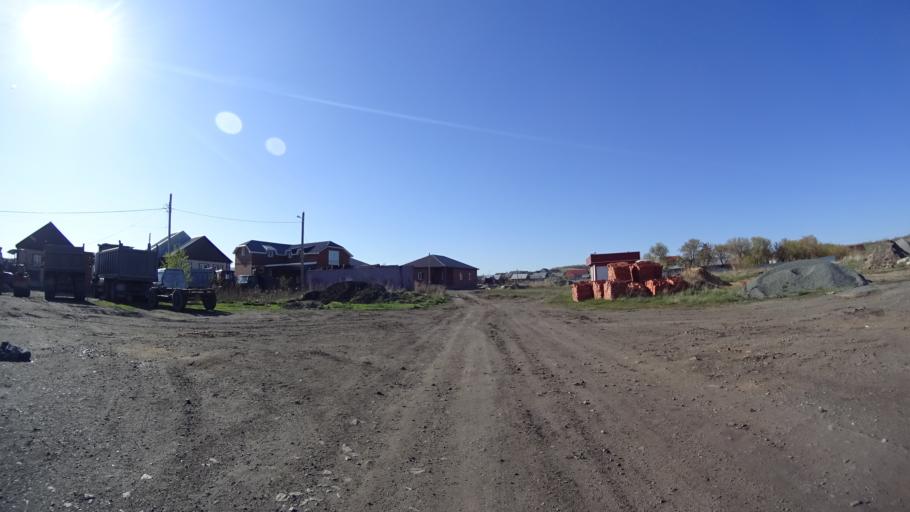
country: RU
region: Chelyabinsk
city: Troitsk
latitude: 54.0945
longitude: 61.5992
